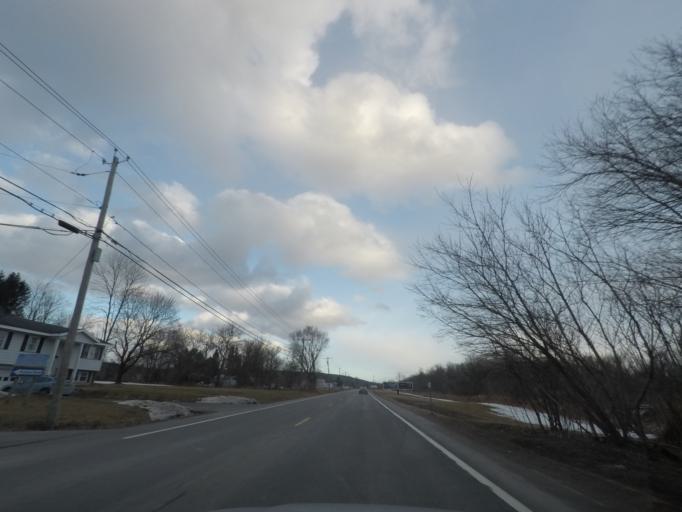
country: US
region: New York
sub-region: Herkimer County
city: Frankfort
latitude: 43.0620
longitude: -75.0881
